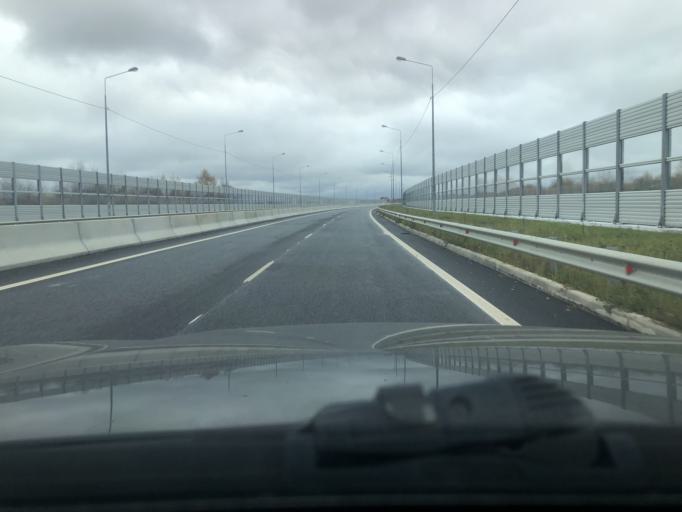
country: RU
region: Moskovskaya
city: Semkhoz
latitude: 56.3172
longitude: 38.0875
